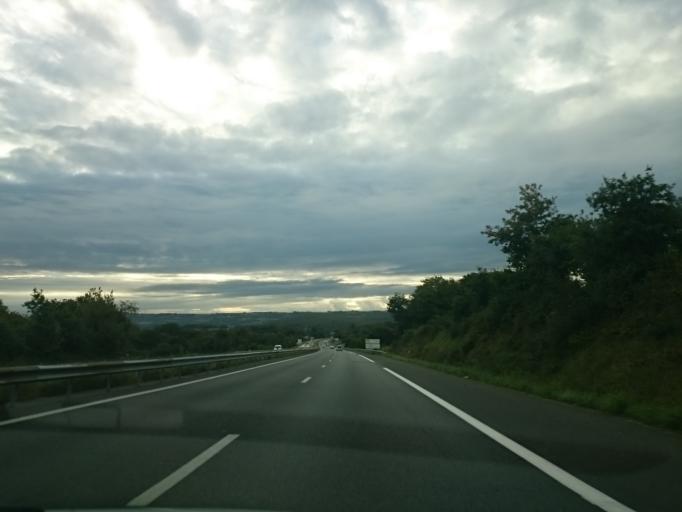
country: FR
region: Brittany
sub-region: Departement du Finistere
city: Le Faou
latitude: 48.3045
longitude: -4.1876
